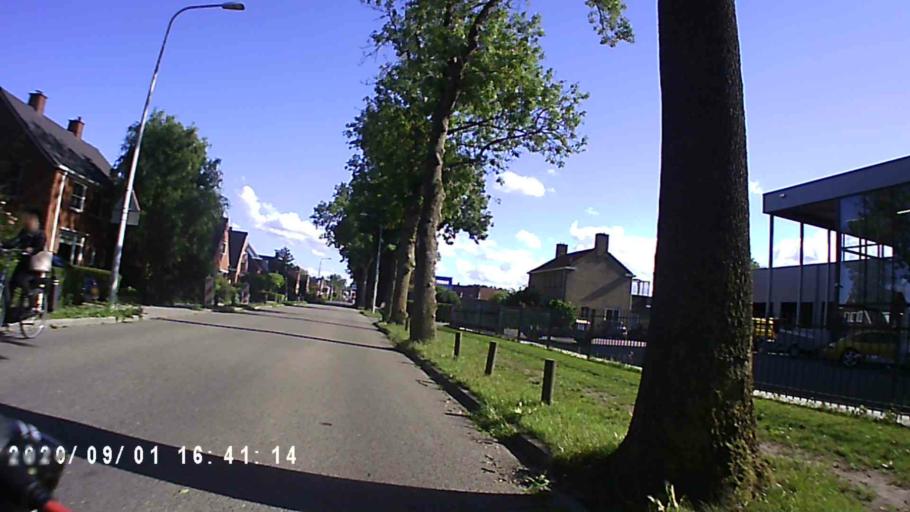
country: NL
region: Groningen
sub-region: Gemeente Groningen
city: Oosterpark
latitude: 53.2288
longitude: 6.5937
